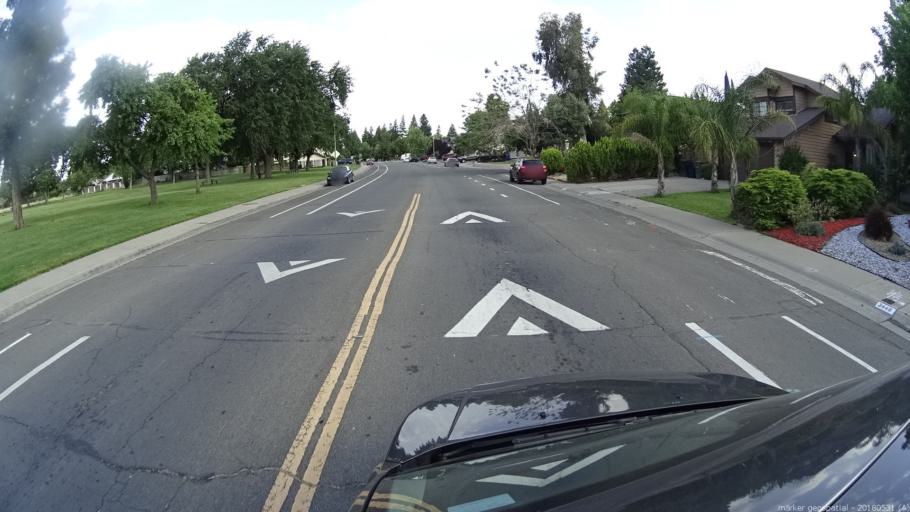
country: US
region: California
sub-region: Sacramento County
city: Sacramento
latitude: 38.6306
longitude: -121.4878
